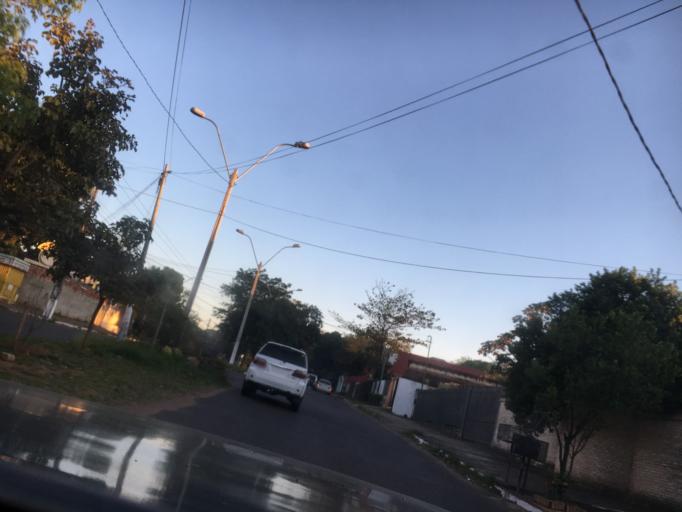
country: PY
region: Central
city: Lambare
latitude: -25.3312
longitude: -57.6088
